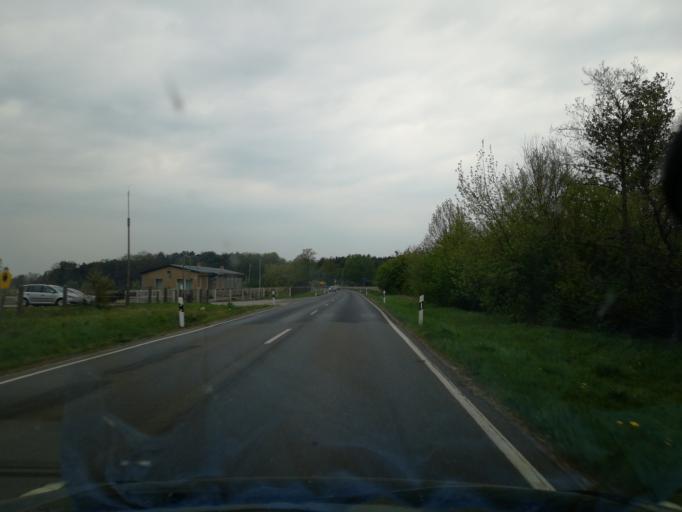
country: DE
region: Brandenburg
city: Calau
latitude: 51.7509
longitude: 13.9385
